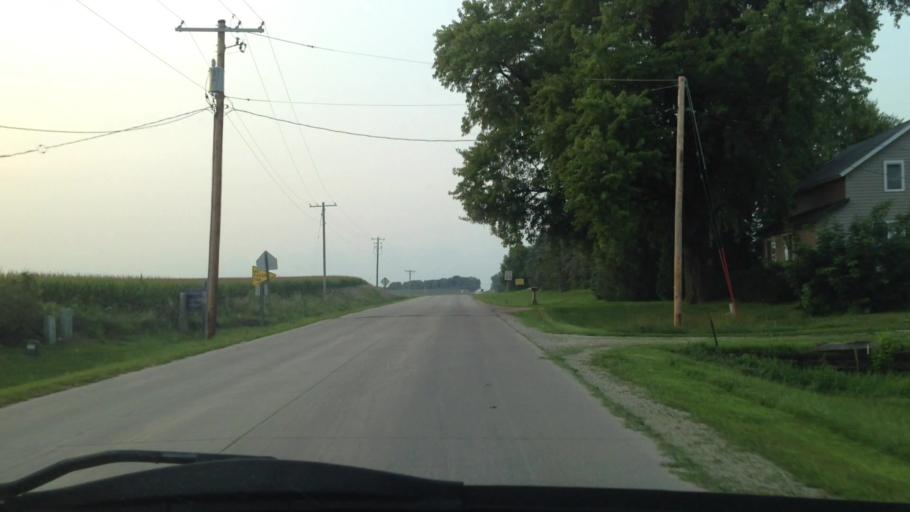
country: US
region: Iowa
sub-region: Linn County
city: Palo
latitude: 42.0965
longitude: -91.8734
